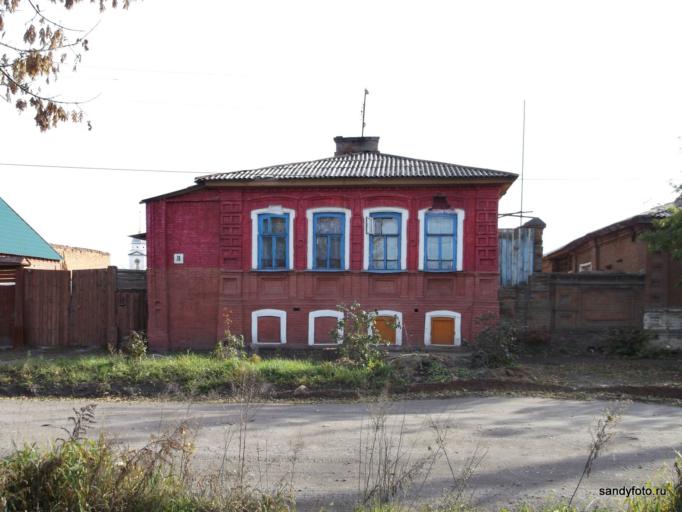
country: RU
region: Chelyabinsk
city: Troitsk
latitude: 54.0796
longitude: 61.5546
